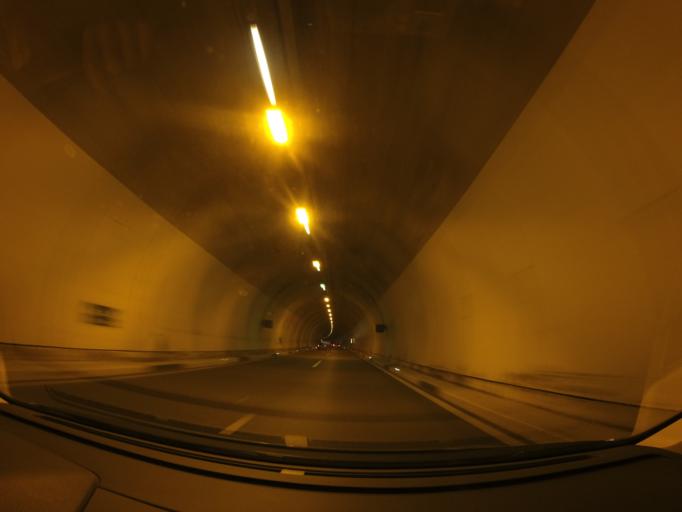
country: CH
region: Saint Gallen
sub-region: Wahlkreis See-Gaster
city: Schmerikon
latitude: 47.2153
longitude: 8.9618
